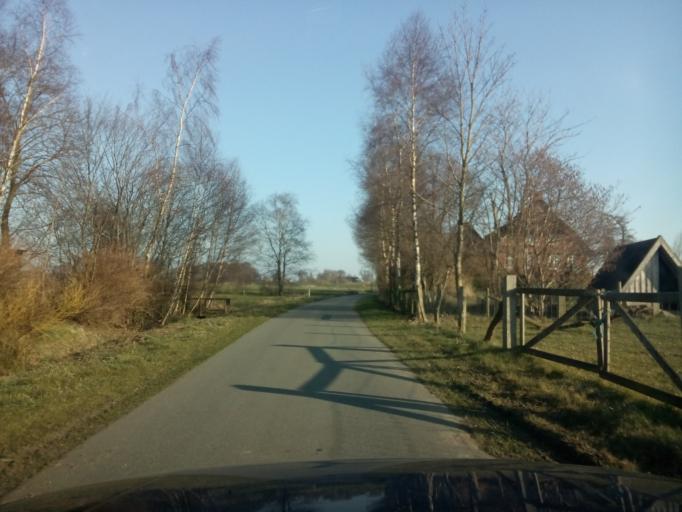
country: DE
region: Lower Saxony
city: Osterholz-Scharmbeck
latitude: 53.1602
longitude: 8.8320
